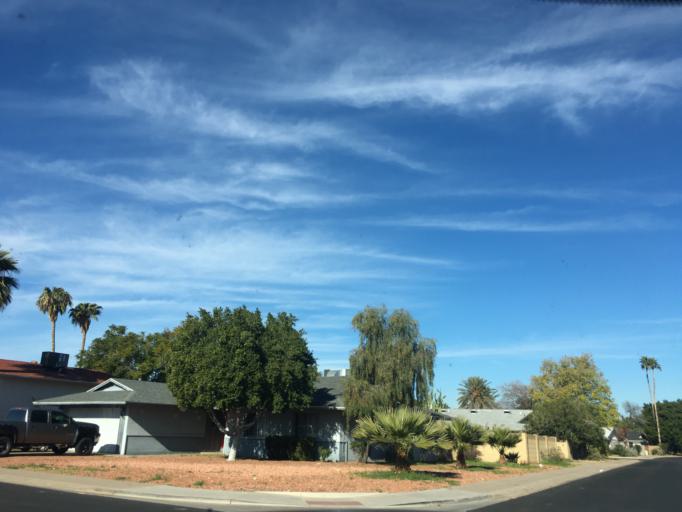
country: US
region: Arizona
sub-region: Maricopa County
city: Tempe
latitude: 33.3883
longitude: -111.9109
